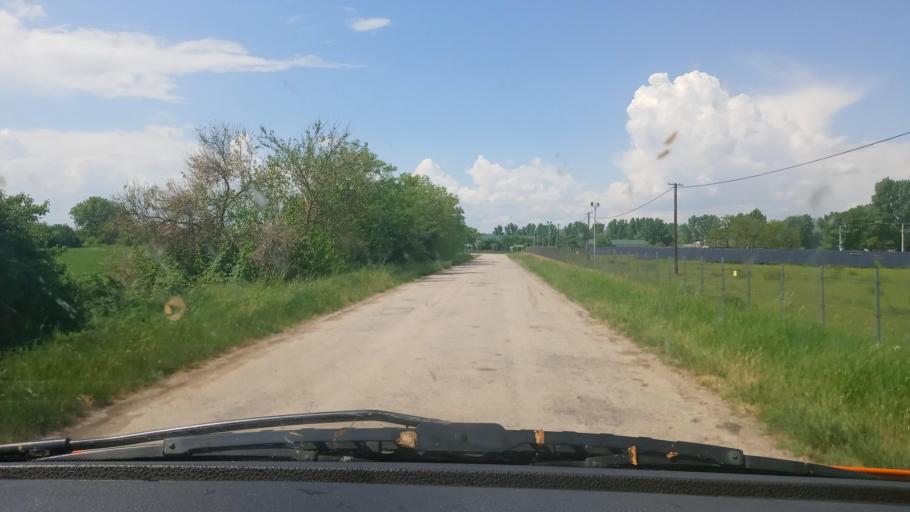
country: HU
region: Baranya
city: Siklos
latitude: 45.8106
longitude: 18.3404
